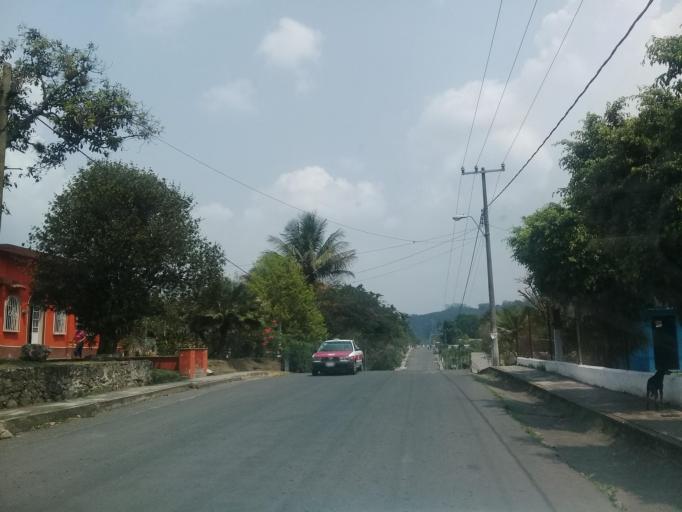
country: MX
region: Veracruz
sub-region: Cordoba
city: San Jose de Tapia
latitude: 18.8180
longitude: -96.9818
